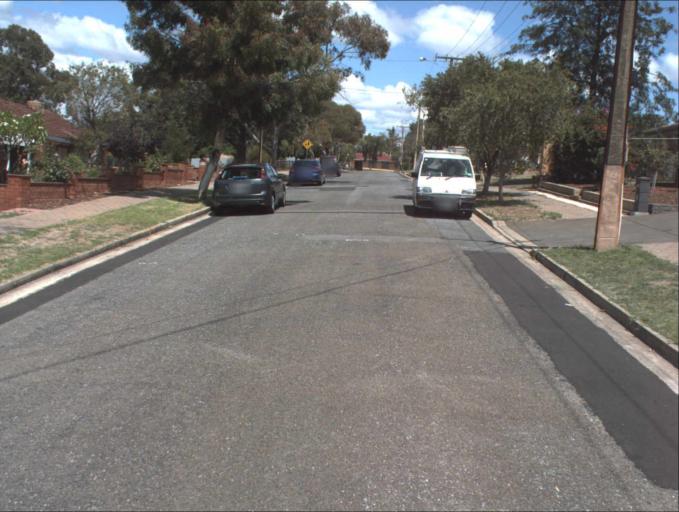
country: AU
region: South Australia
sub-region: Port Adelaide Enfield
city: Gilles Plains
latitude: -34.8432
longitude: 138.6580
